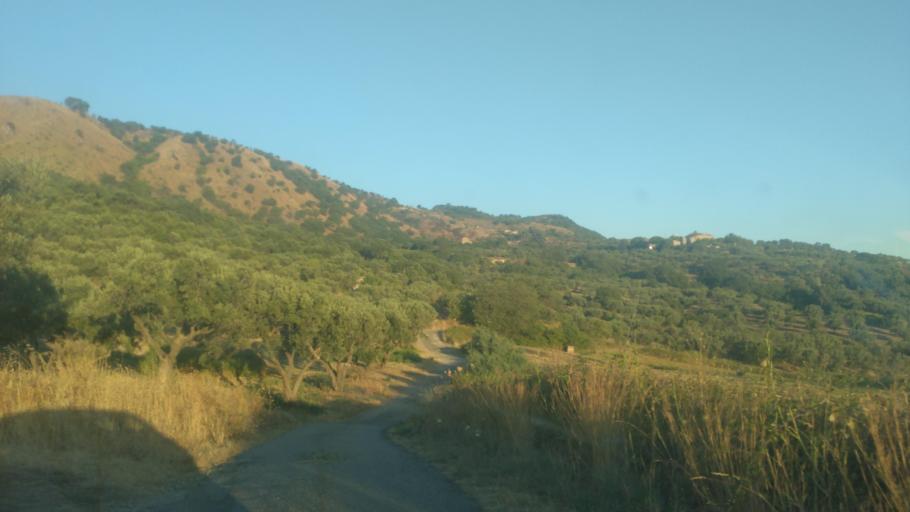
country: IT
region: Calabria
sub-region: Provincia di Catanzaro
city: Staletti
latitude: 38.7724
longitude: 16.5520
